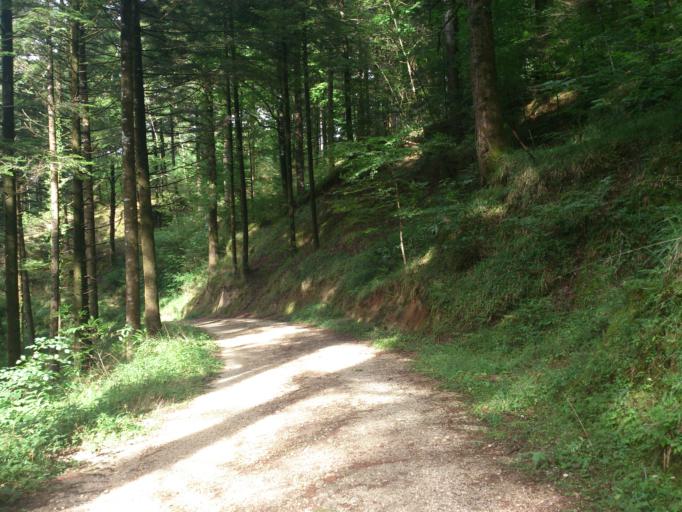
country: IT
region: Calabria
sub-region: Provincia di Vibo-Valentia
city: Serra San Bruno
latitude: 38.5517
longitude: 16.3106
